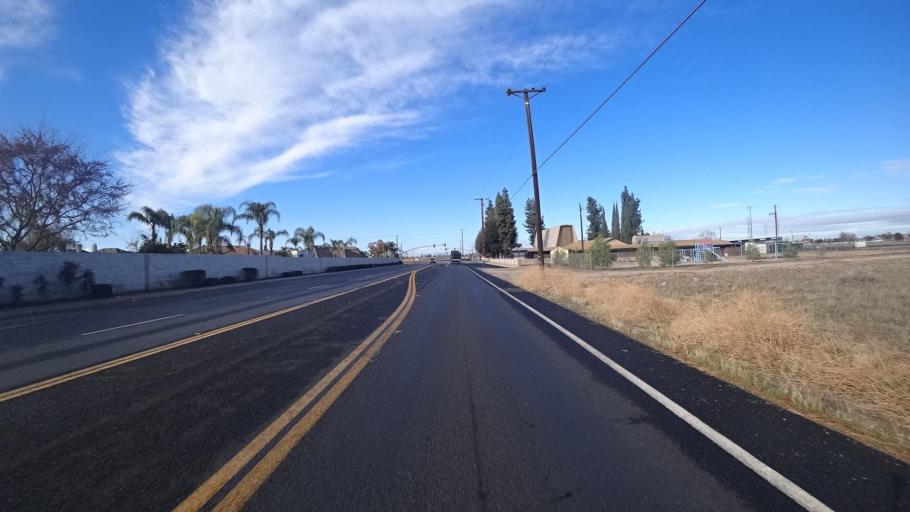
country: US
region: California
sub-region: Kern County
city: Rosedale
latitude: 35.3836
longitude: -119.1791
